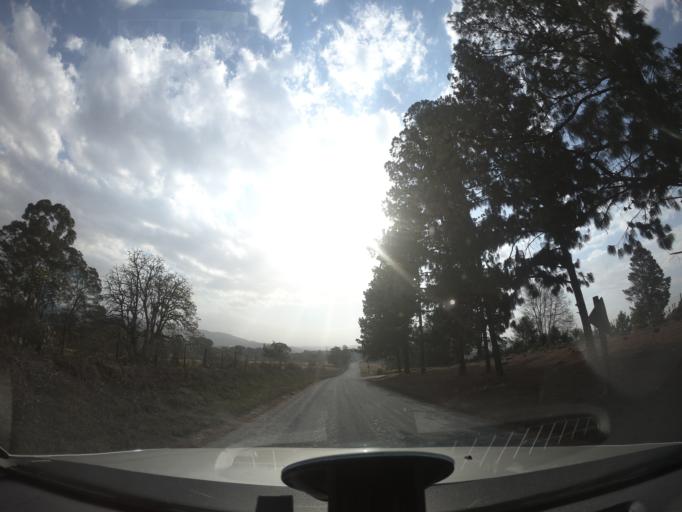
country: ZA
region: KwaZulu-Natal
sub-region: uMgungundlovu District Municipality
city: Howick
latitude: -29.4354
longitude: 30.1136
